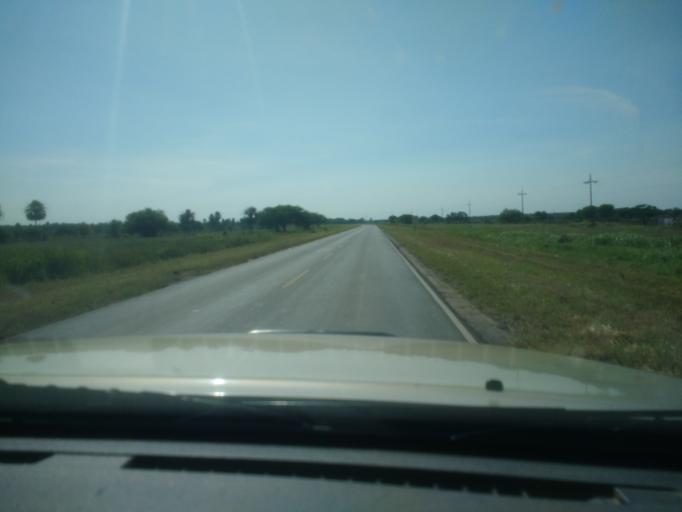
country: PY
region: Presidente Hayes
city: Benjamin Aceval
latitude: -24.9192
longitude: -57.6043
